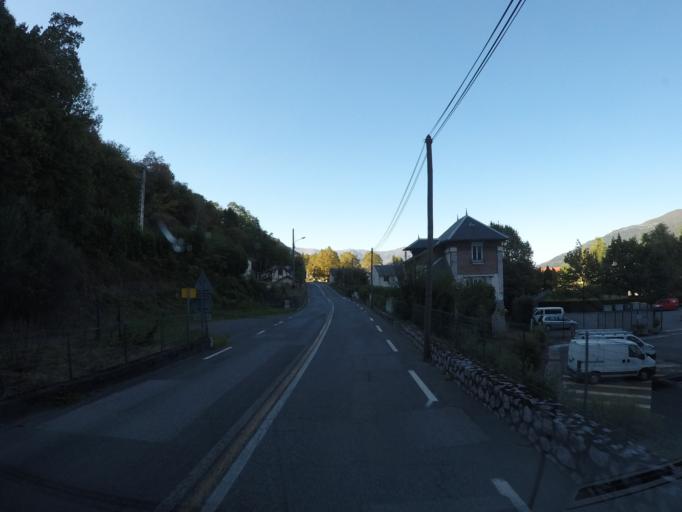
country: FR
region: Midi-Pyrenees
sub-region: Departement des Hautes-Pyrenees
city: Pierrefitte-Nestalas
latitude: 42.9527
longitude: -0.0700
